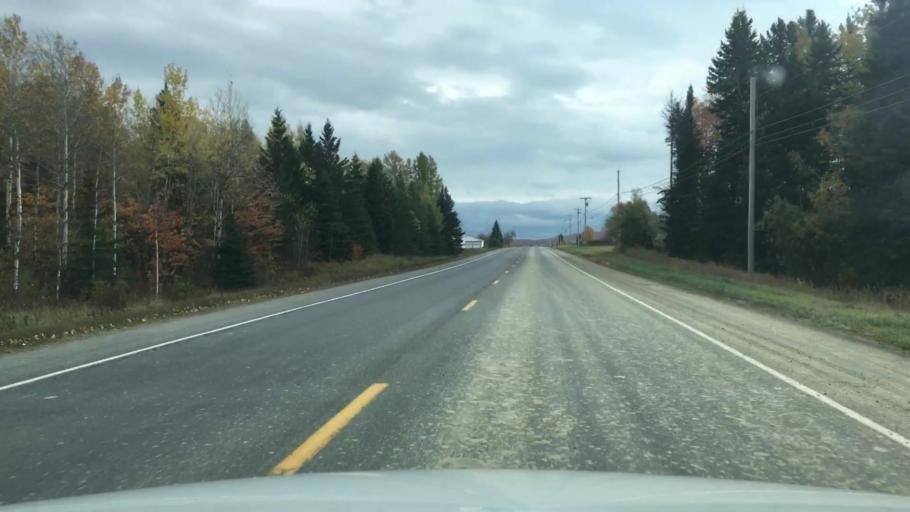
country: US
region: Maine
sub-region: Aroostook County
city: Easton
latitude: 46.5605
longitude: -67.9436
